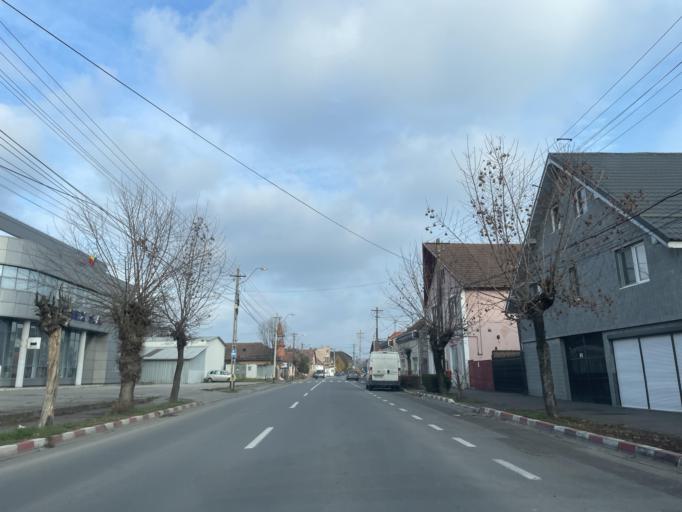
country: RO
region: Mures
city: Reghin-Sat
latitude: 46.7796
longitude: 24.7167
